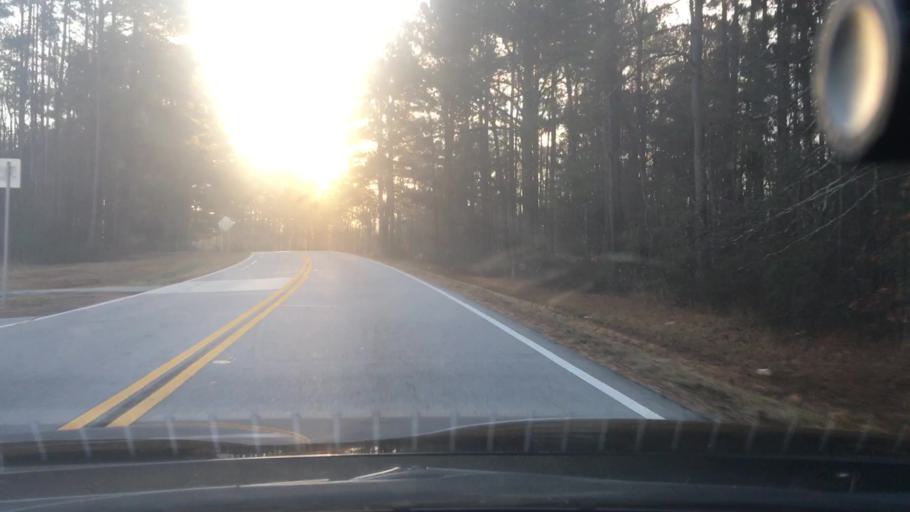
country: US
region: Georgia
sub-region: Coweta County
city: Senoia
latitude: 33.3283
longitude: -84.5058
